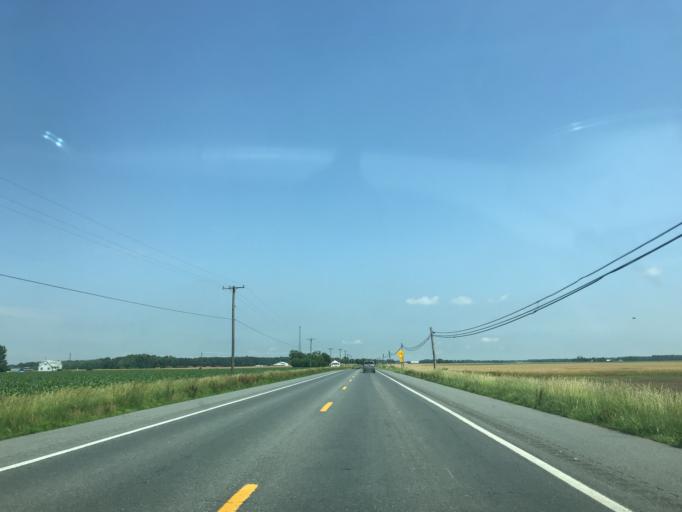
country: US
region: Maryland
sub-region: Dorchester County
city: Hurlock
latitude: 38.5875
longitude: -75.8673
